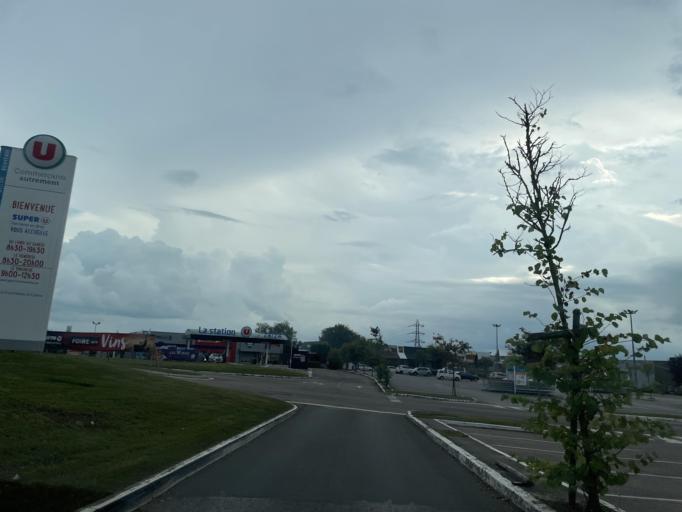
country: FR
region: Haute-Normandie
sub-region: Departement de la Seine-Maritime
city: Gournay-en-Bray
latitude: 49.4790
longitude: 1.7397
